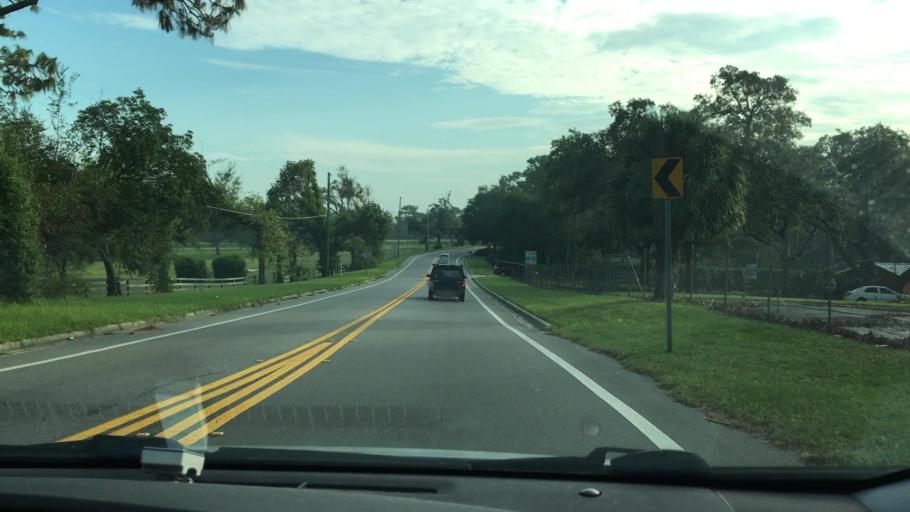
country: US
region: Florida
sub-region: Seminole County
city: Longwood
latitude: 28.7135
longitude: -81.3504
